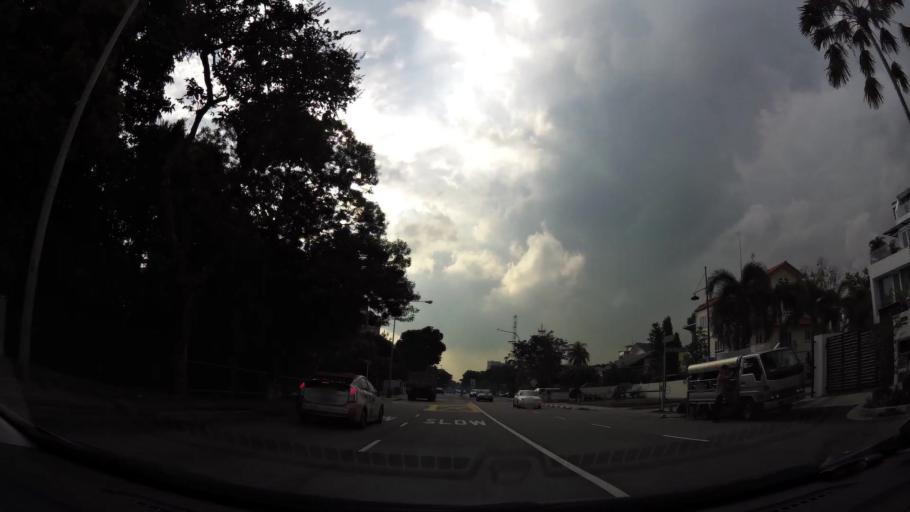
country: SG
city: Singapore
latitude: 1.3145
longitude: 103.9366
